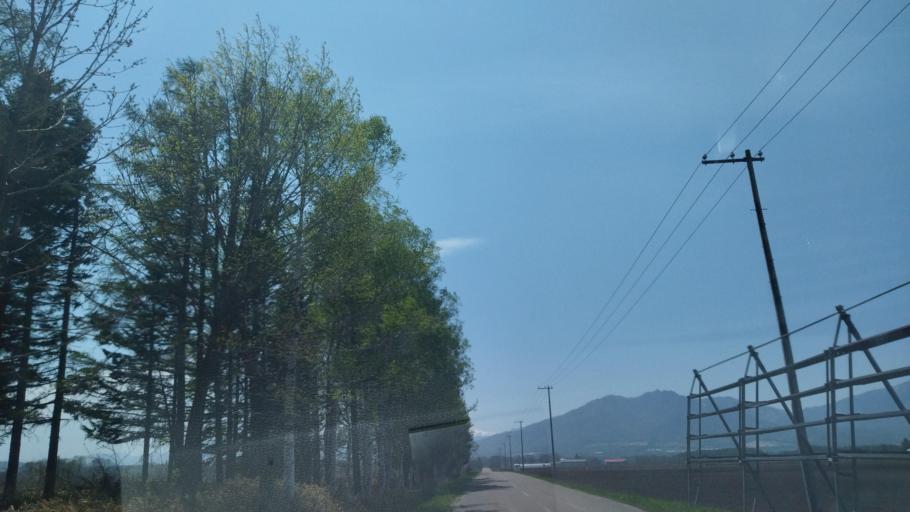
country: JP
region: Hokkaido
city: Obihiro
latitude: 42.9051
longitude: 142.9875
